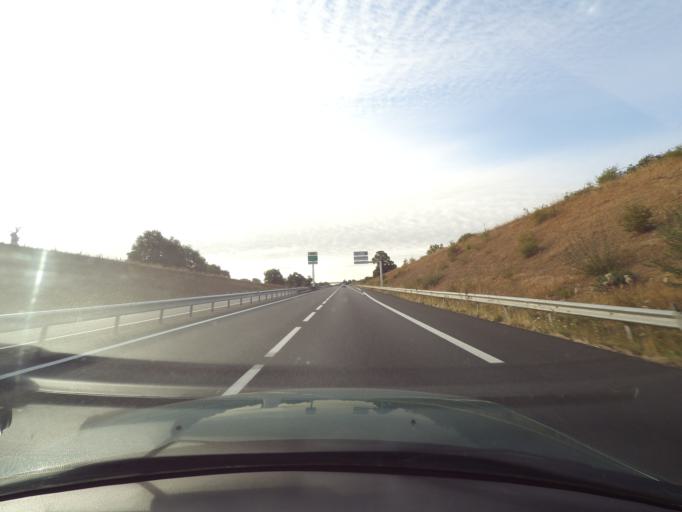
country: FR
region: Pays de la Loire
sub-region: Departement de Maine-et-Loire
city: La Tessoualle
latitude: 46.9917
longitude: -0.8493
